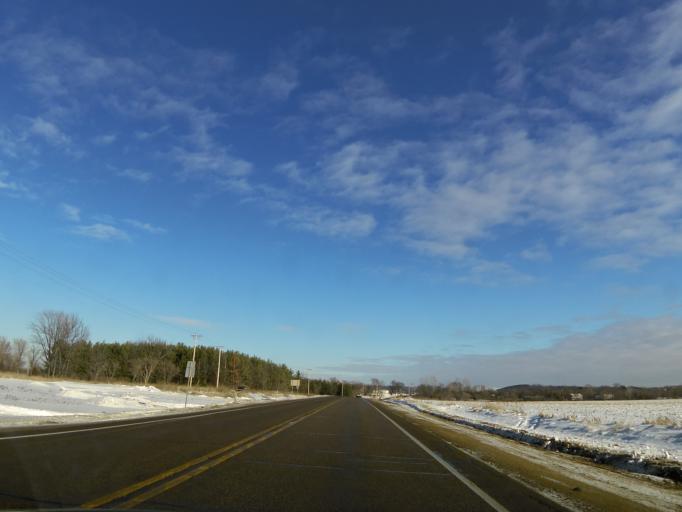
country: US
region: Wisconsin
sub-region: Saint Croix County
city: North Hudson
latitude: 44.9884
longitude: -92.6768
